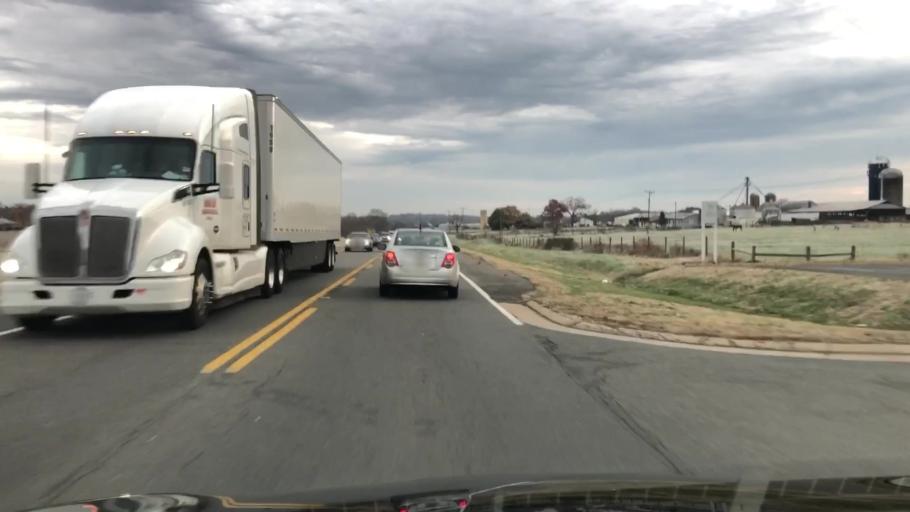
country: US
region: Virginia
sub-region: Fauquier County
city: Bealeton
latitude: 38.6018
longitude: -77.7237
